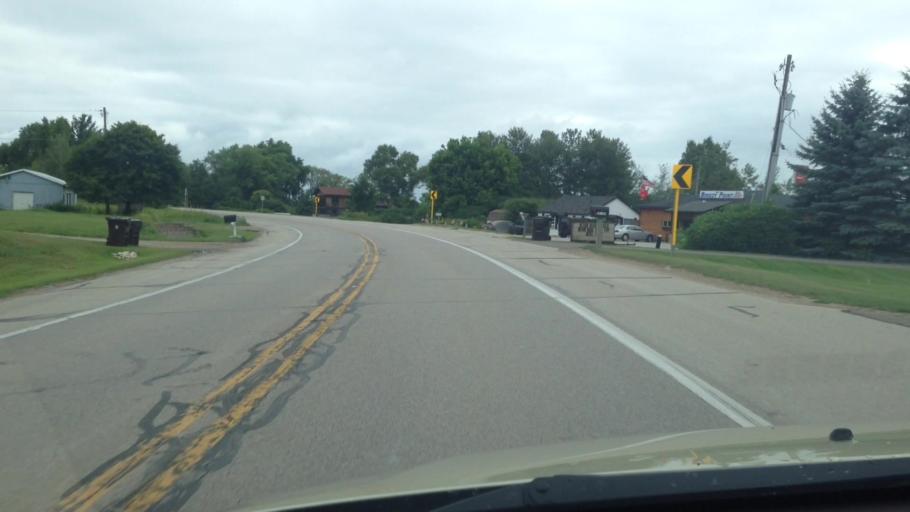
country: US
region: Michigan
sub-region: Delta County
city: Escanaba
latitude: 45.6878
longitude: -87.1020
